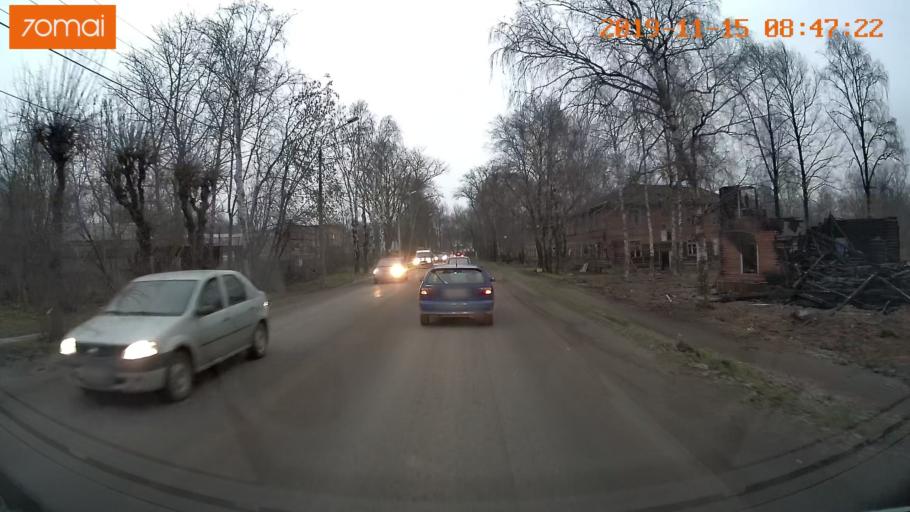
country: RU
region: Vologda
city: Cherepovets
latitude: 59.1206
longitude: 37.9151
